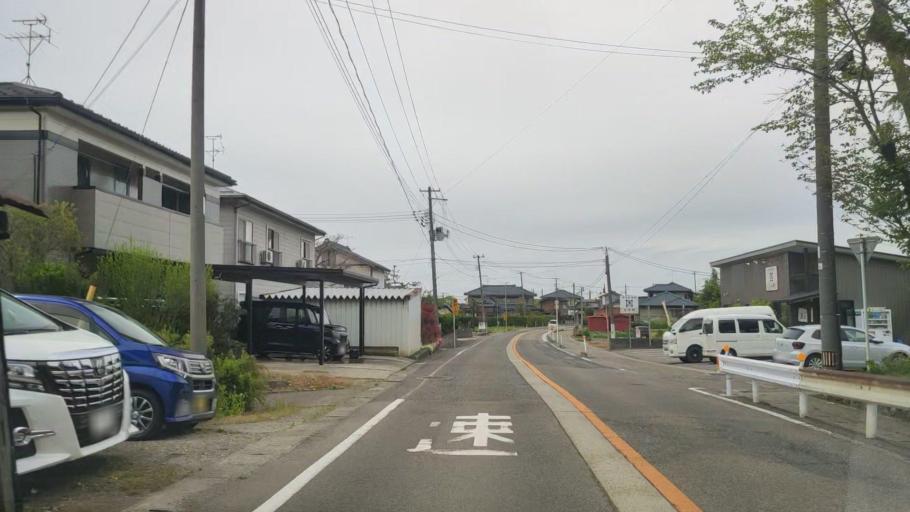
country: JP
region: Niigata
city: Kamo
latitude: 37.7146
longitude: 139.0734
